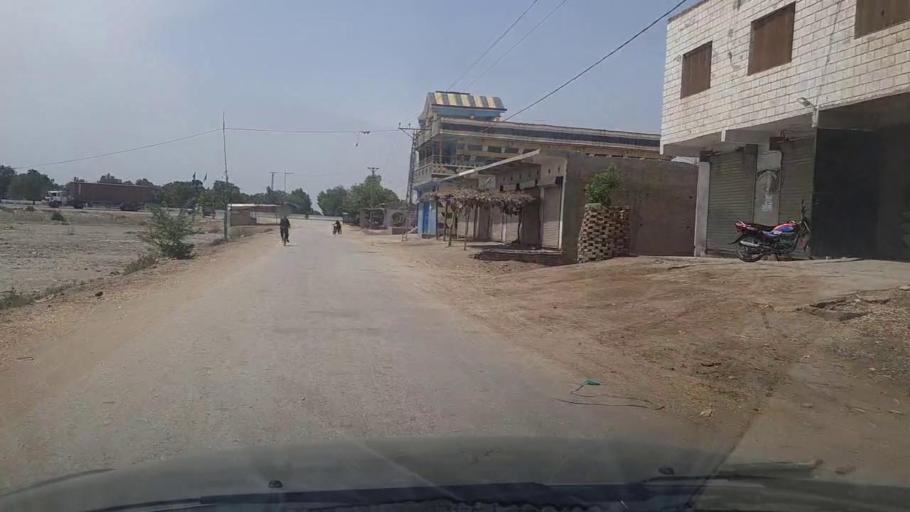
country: PK
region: Sindh
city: Bhiria
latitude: 26.9109
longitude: 68.1880
